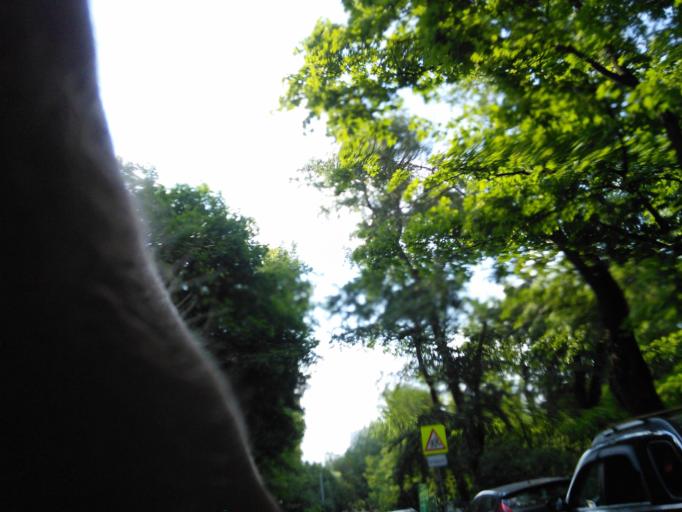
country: RU
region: Moskovskaya
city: Bogorodskoye
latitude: 55.8148
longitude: 37.7114
